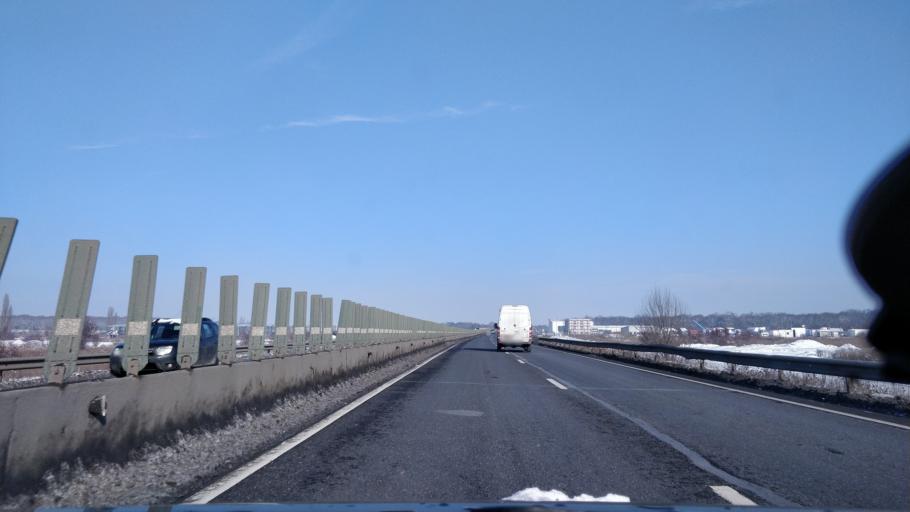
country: RO
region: Ilfov
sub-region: Comuna Chitila
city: Chitila
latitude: 44.5040
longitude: 26.0037
